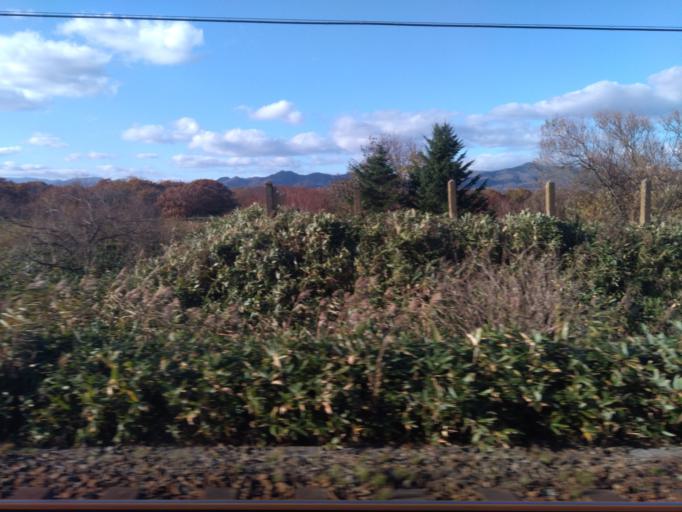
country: JP
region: Hokkaido
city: Niseko Town
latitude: 42.5323
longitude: 140.3961
